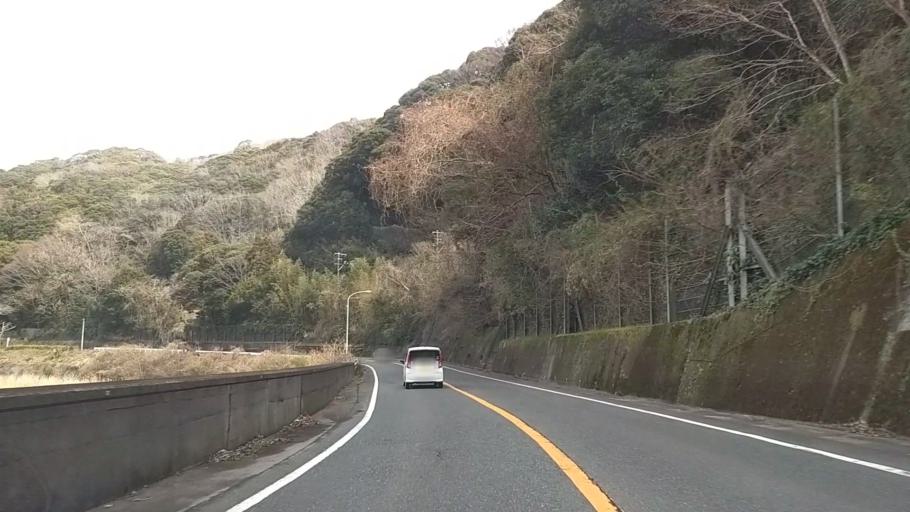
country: JP
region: Shizuoka
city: Shimoda
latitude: 34.7130
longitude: 138.9472
